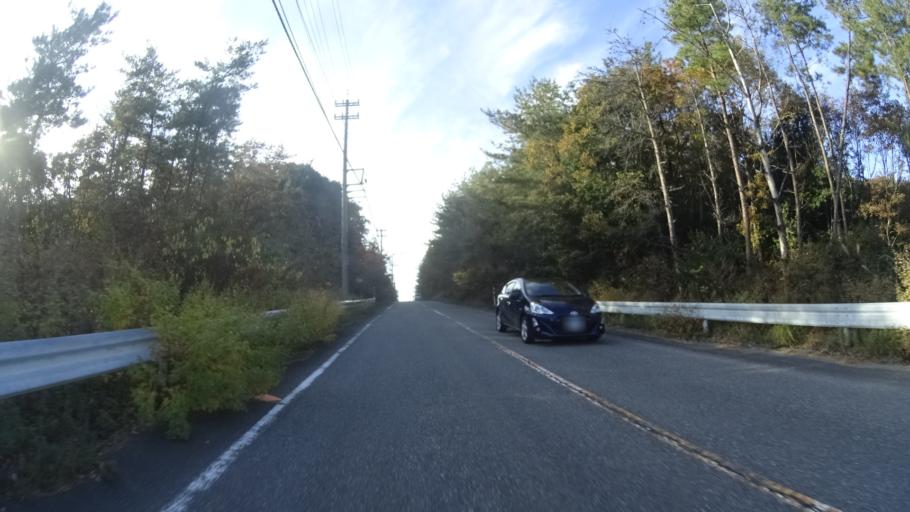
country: JP
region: Ishikawa
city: Hakui
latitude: 37.0694
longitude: 136.7480
